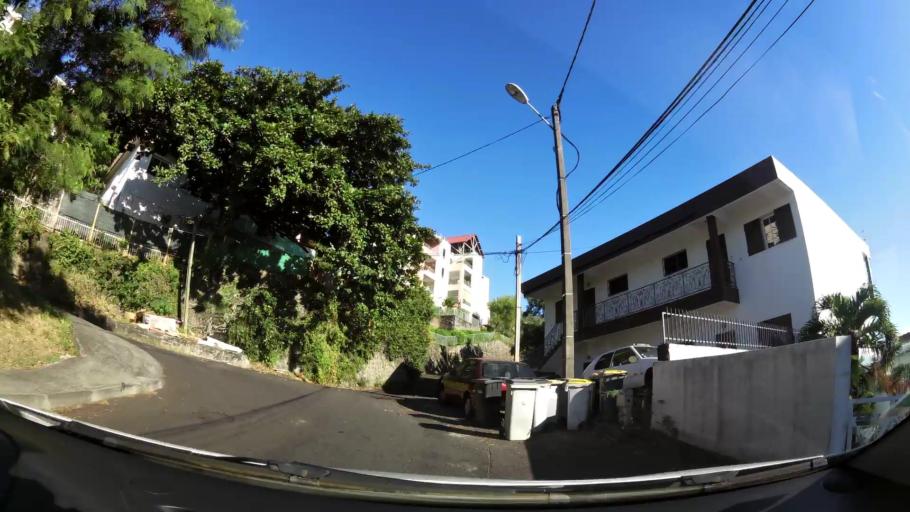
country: RE
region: Reunion
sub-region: Reunion
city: Saint-Denis
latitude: -20.8926
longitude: 55.4475
